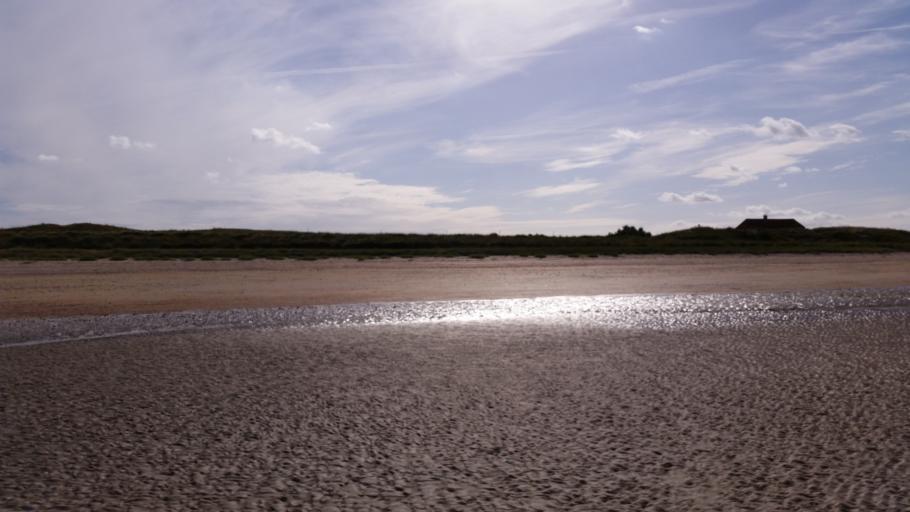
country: FR
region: Lower Normandy
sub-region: Departement de la Manche
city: Sainte-Mere-Eglise
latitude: 49.4479
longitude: -1.2116
